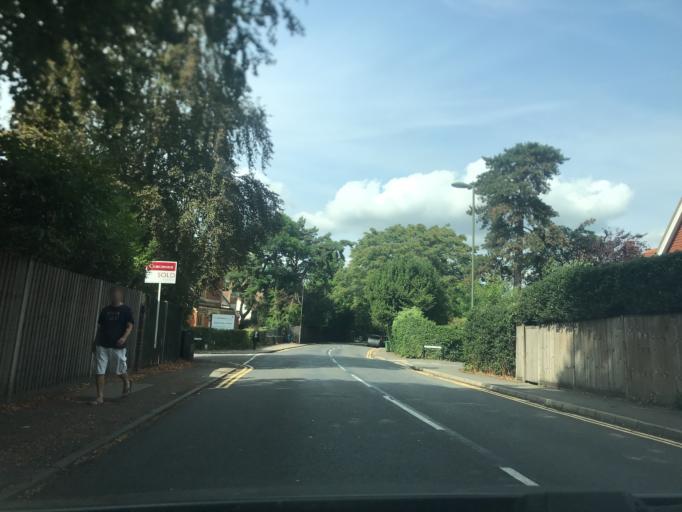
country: GB
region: England
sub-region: Surrey
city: Weybridge
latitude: 51.3690
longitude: -0.4617
